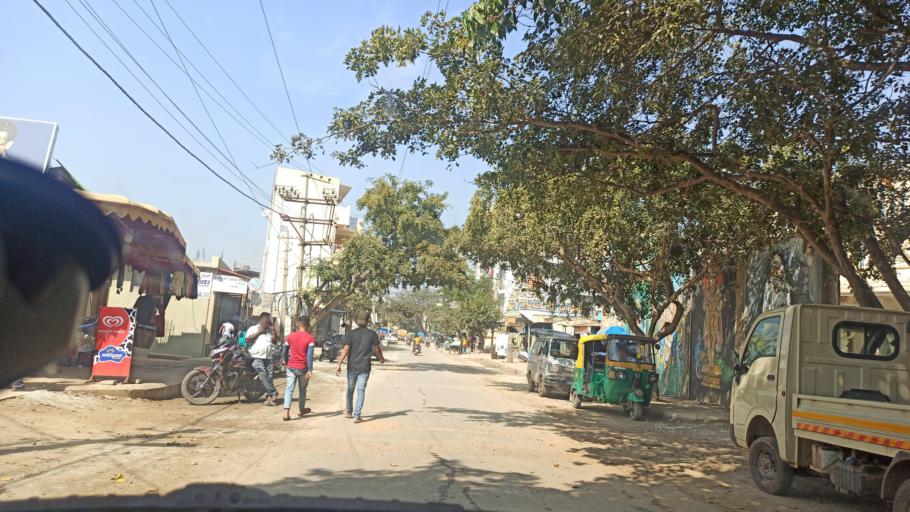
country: IN
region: Karnataka
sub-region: Bangalore Urban
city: Bangalore
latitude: 12.9252
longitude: 77.6936
